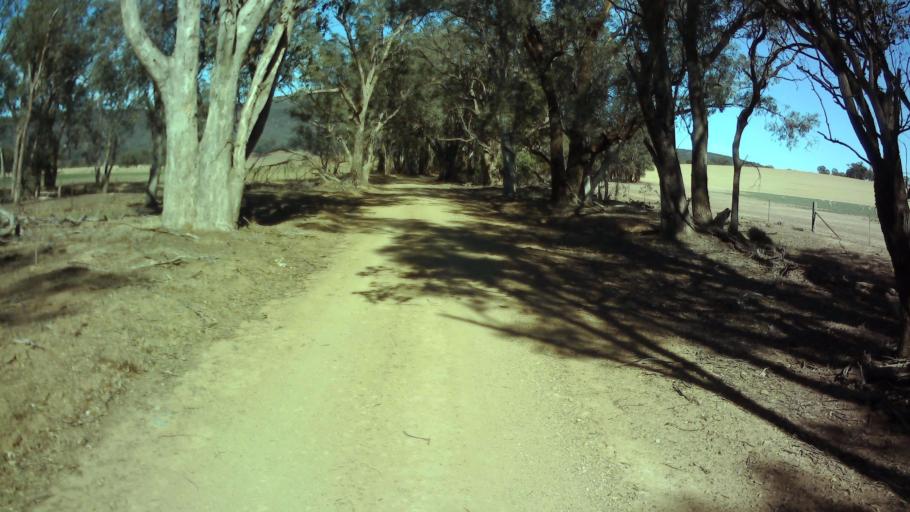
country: AU
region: New South Wales
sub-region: Weddin
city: Grenfell
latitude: -33.9011
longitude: 148.0264
